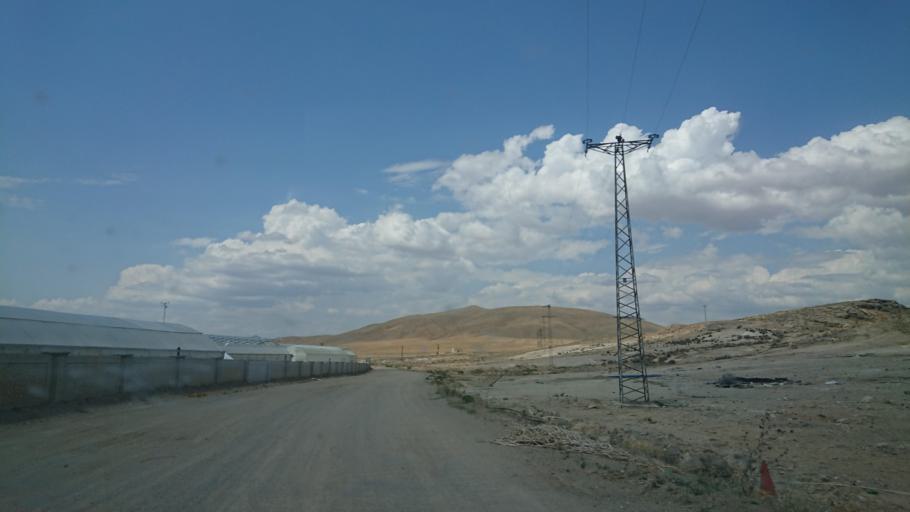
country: TR
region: Aksaray
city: Sariyahsi
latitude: 39.0000
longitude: 33.9120
